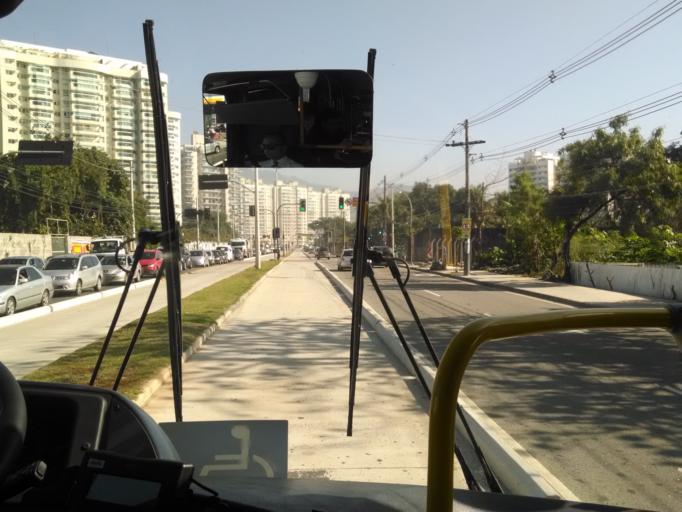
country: BR
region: Rio de Janeiro
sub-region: Nilopolis
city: Nilopolis
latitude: -22.9724
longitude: -43.3865
